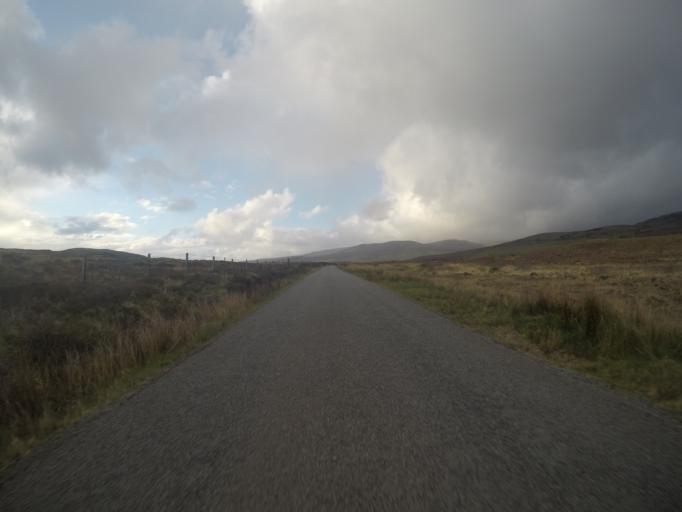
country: GB
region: Scotland
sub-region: Highland
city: Isle of Skye
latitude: 57.4587
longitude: -6.2969
